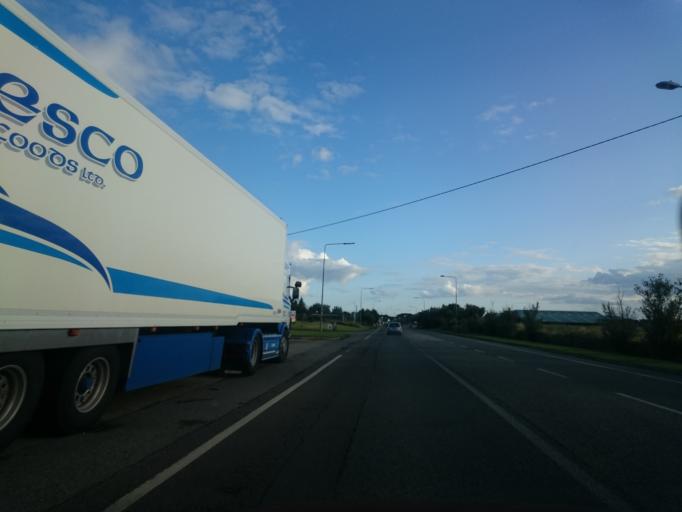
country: IE
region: Leinster
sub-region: Loch Garman
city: Ballygerry
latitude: 52.2471
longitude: -6.3450
